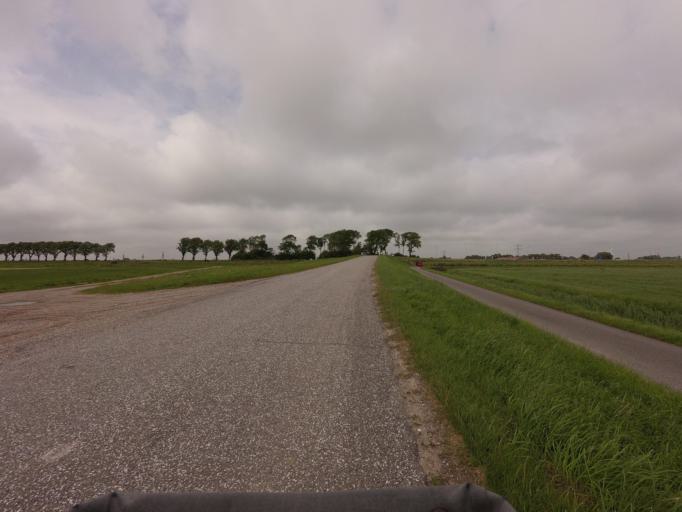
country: NL
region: North Holland
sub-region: Gemeente Schagen
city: Schagen
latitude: 52.7990
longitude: 4.8259
